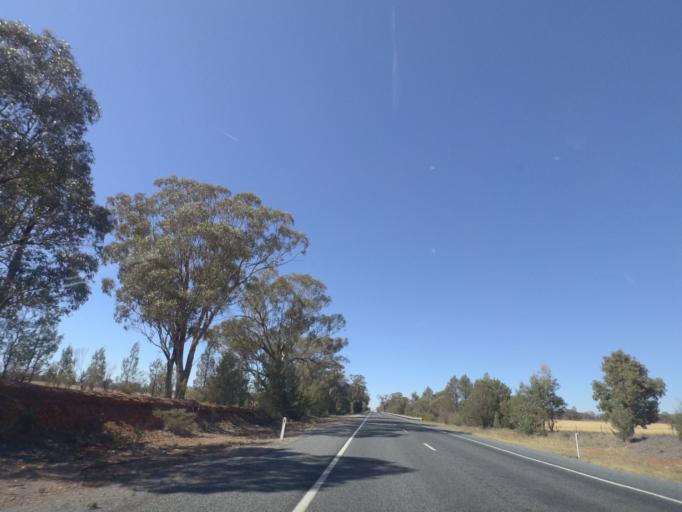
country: AU
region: New South Wales
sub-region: Bland
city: West Wyalong
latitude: -34.1630
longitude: 147.1164
